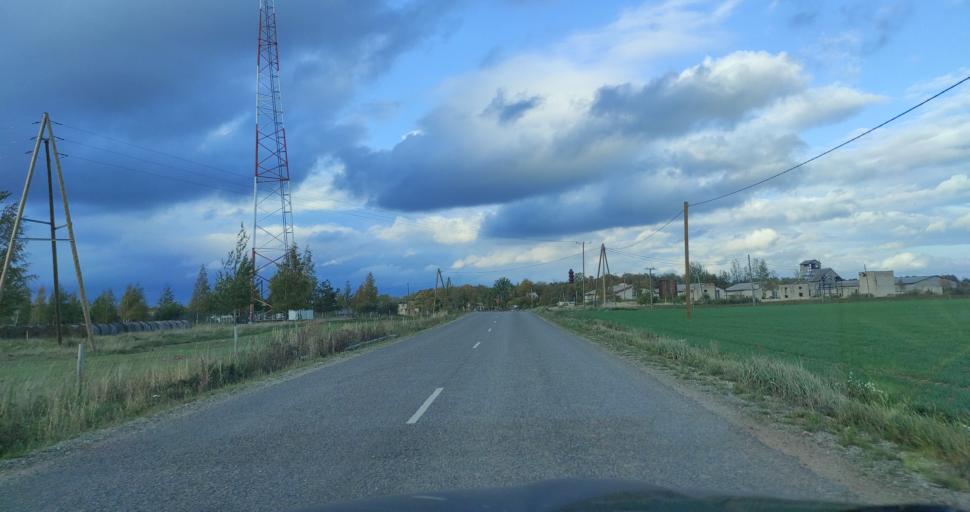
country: LV
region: Talsu Rajons
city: Sabile
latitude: 56.9438
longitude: 22.3978
